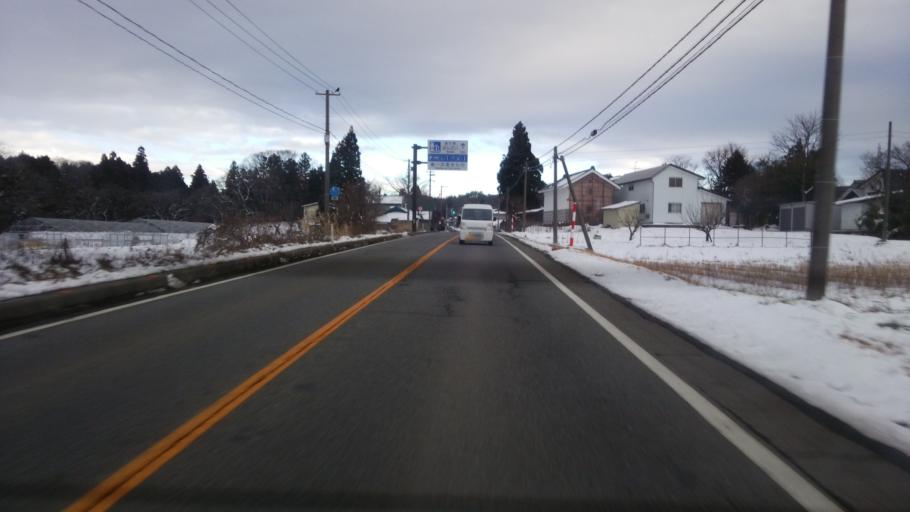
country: JP
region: Fukushima
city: Kitakata
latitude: 37.5663
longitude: 139.9675
